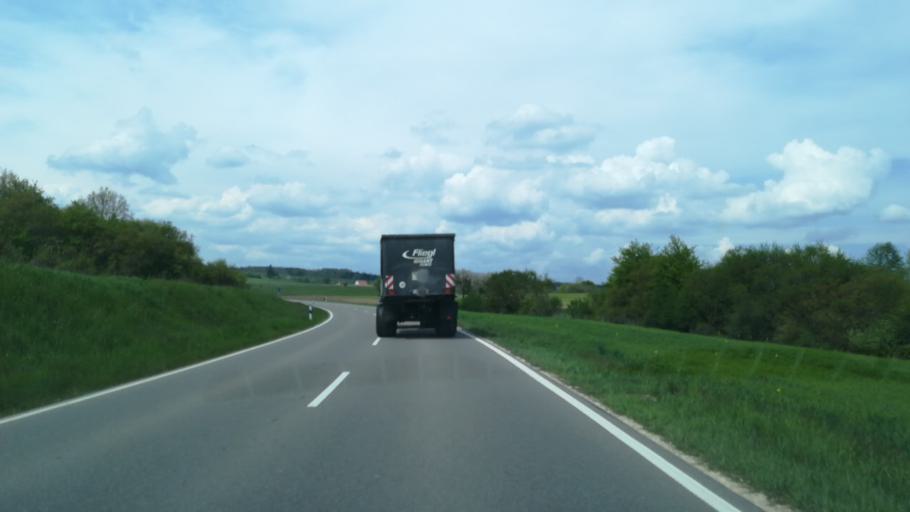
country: DE
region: Baden-Wuerttemberg
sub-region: Tuebingen Region
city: Messkirch
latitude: 48.0159
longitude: 9.1115
